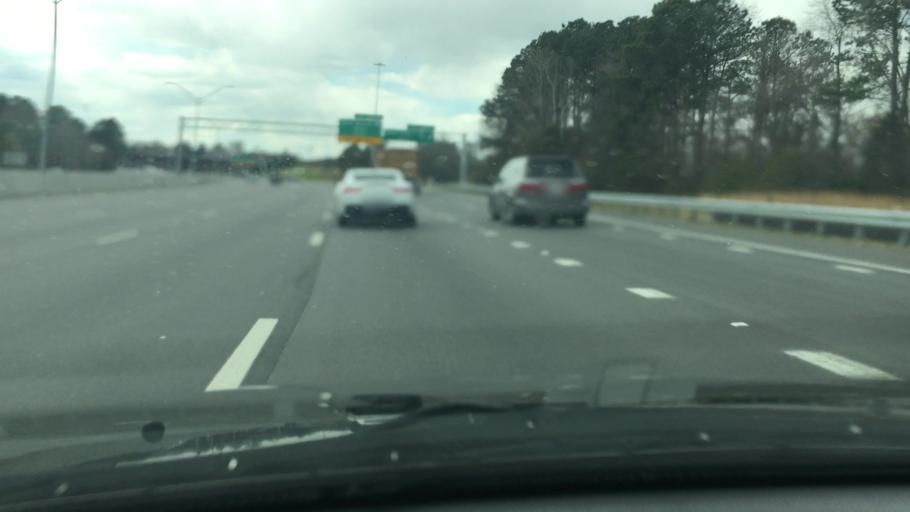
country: US
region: North Carolina
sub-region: Wake County
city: Raleigh
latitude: 35.7580
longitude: -78.6077
